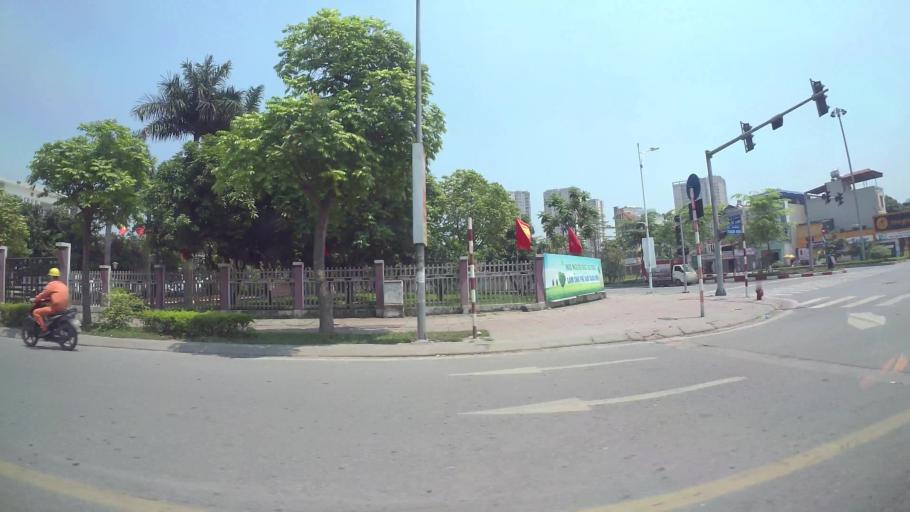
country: VN
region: Ha Noi
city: Trau Quy
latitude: 21.0231
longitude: 105.9055
